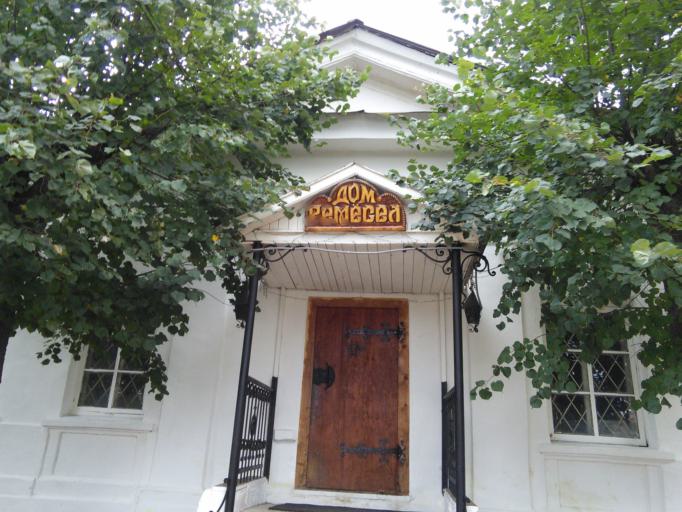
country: RU
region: Jaroslavl
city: Myshkin
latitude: 57.7880
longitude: 38.4594
